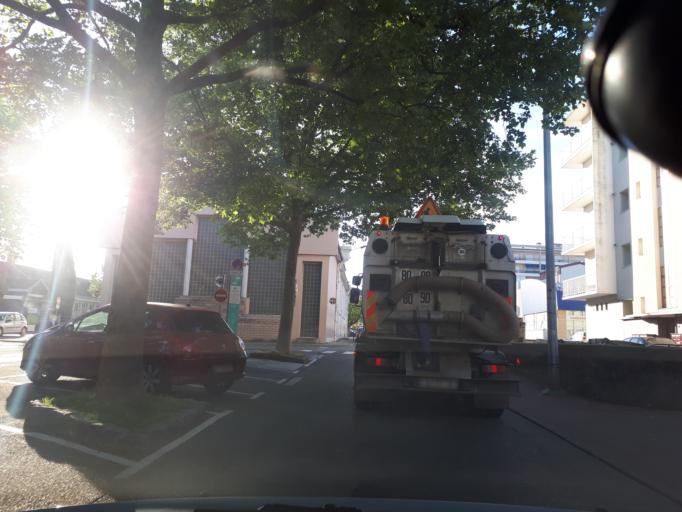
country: FR
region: Rhone-Alpes
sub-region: Departement de l'Isere
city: Bourgoin
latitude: 45.5903
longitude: 5.2802
